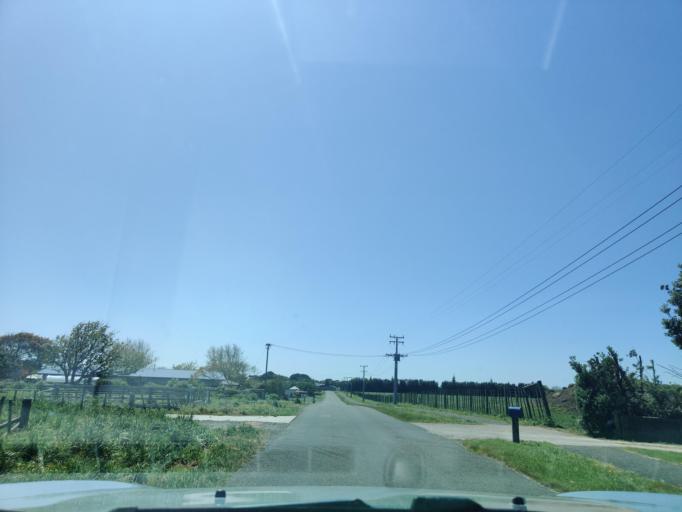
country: NZ
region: Taranaki
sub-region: South Taranaki District
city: Hawera
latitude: -39.5962
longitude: 174.2674
